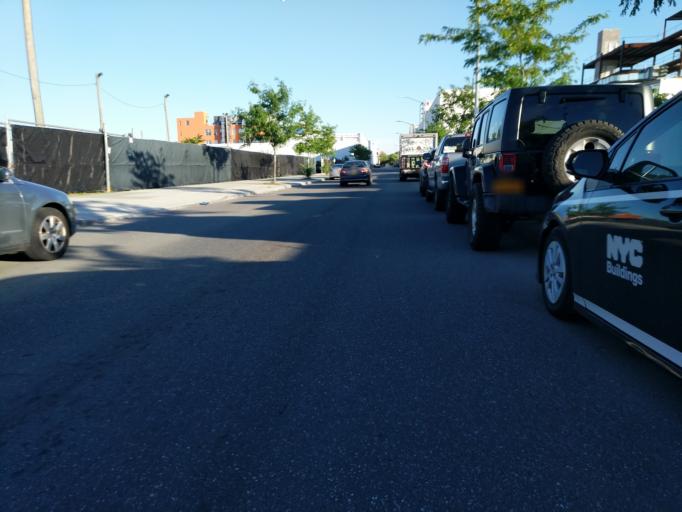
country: US
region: New York
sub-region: Queens County
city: Long Island City
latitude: 40.7315
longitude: -73.9436
